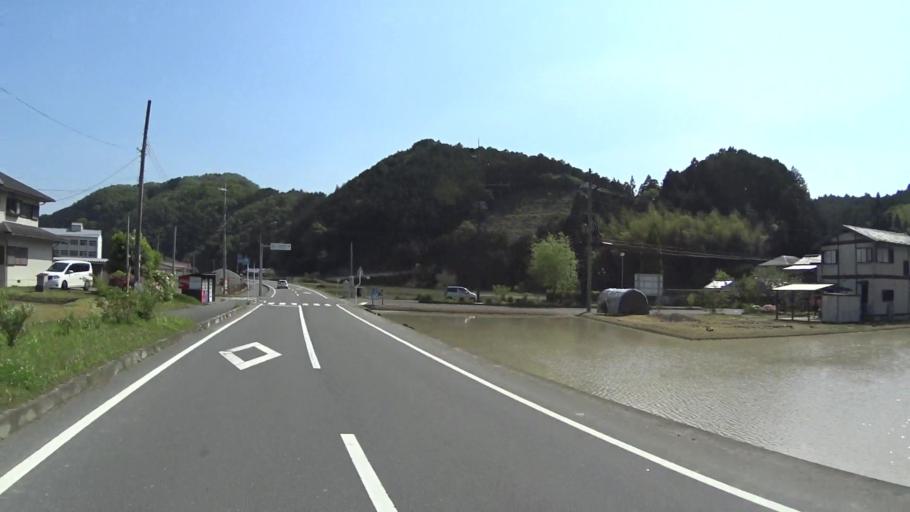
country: JP
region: Kyoto
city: Kameoka
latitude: 35.1333
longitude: 135.4931
